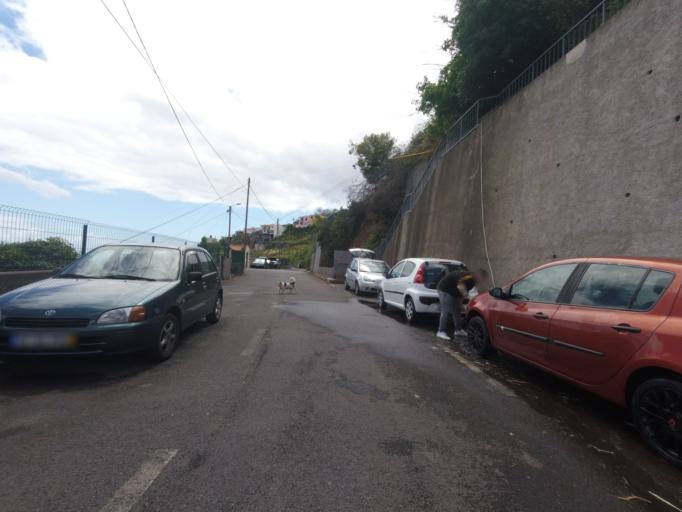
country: PT
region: Madeira
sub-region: Funchal
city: Nossa Senhora do Monte
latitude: 32.6709
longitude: -16.9192
